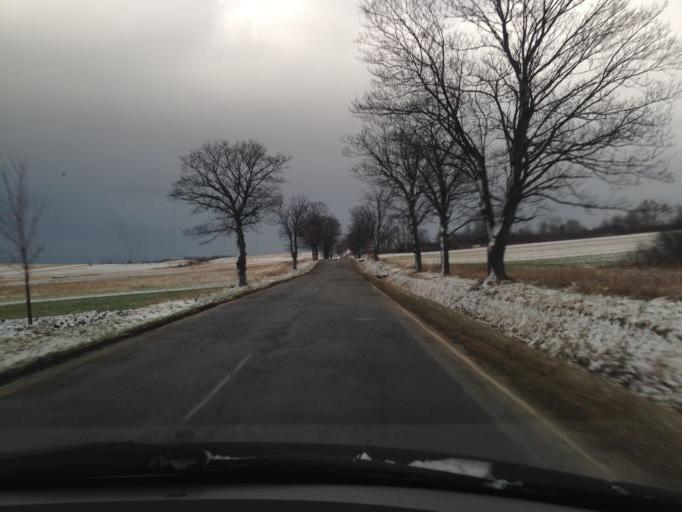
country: PL
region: Subcarpathian Voivodeship
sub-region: Powiat jasielski
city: Osiek Jasielski
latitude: 49.6104
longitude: 21.4931
